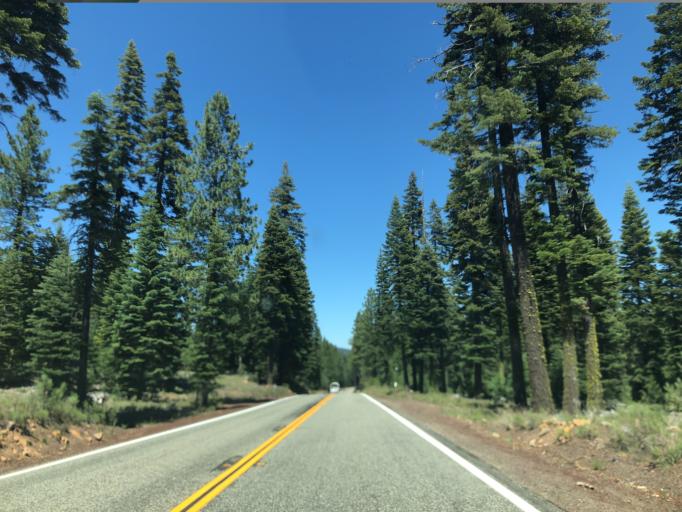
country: US
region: California
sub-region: Shasta County
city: Burney
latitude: 40.5980
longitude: -121.5341
